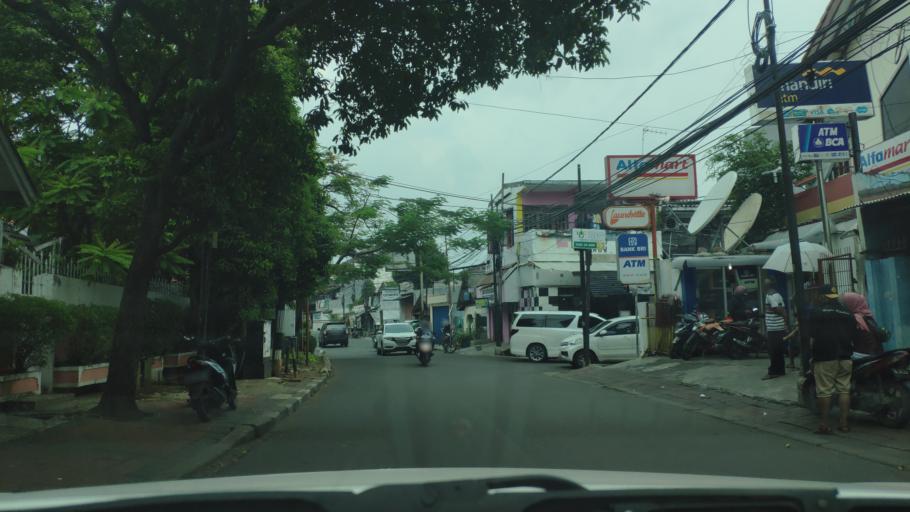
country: ID
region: Jakarta Raya
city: Jakarta
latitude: -6.1950
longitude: 106.7950
